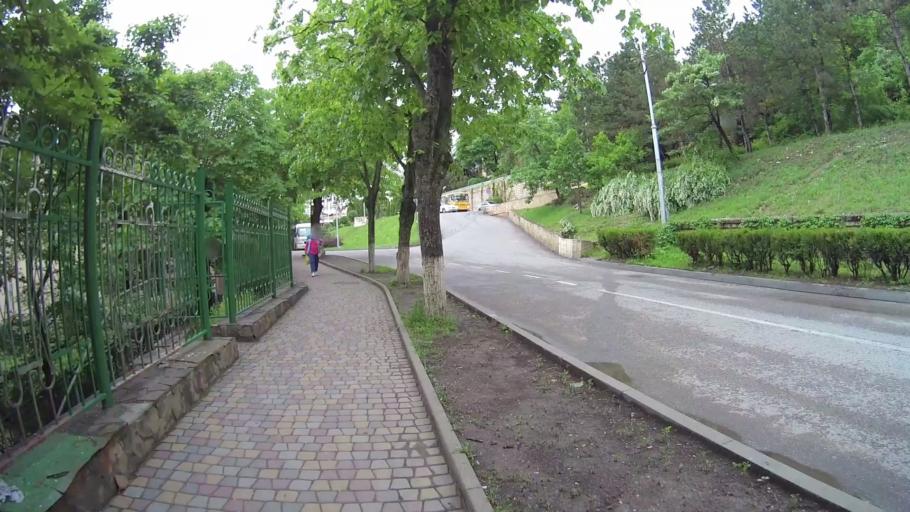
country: RU
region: Stavropol'skiy
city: Goryachevodskiy
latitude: 44.0452
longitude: 43.0984
